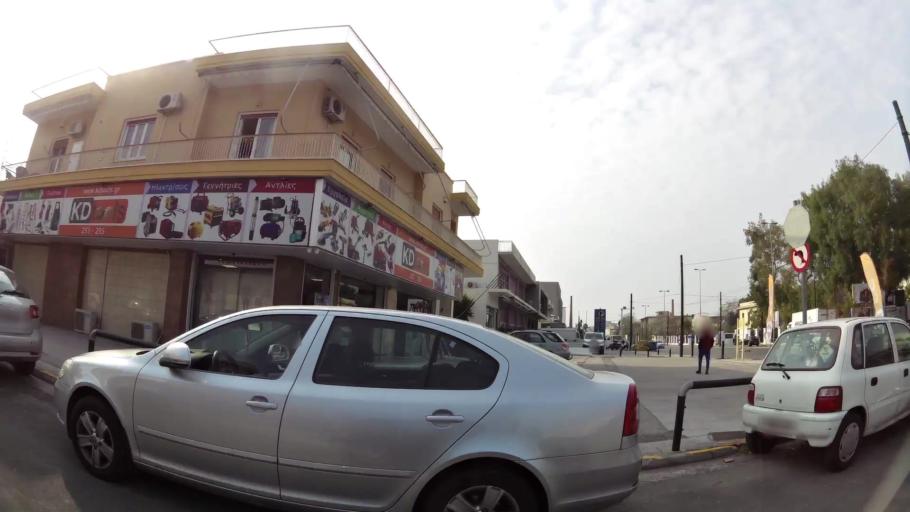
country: GR
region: Attica
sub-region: Nomarchia Athinas
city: Tavros
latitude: 37.9627
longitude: 23.6915
